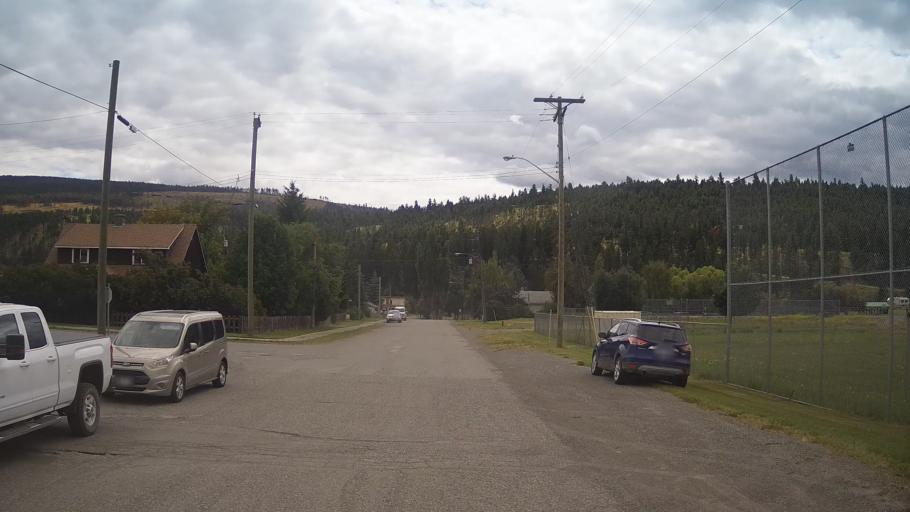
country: CA
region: British Columbia
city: Cache Creek
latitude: 51.0903
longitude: -121.5869
